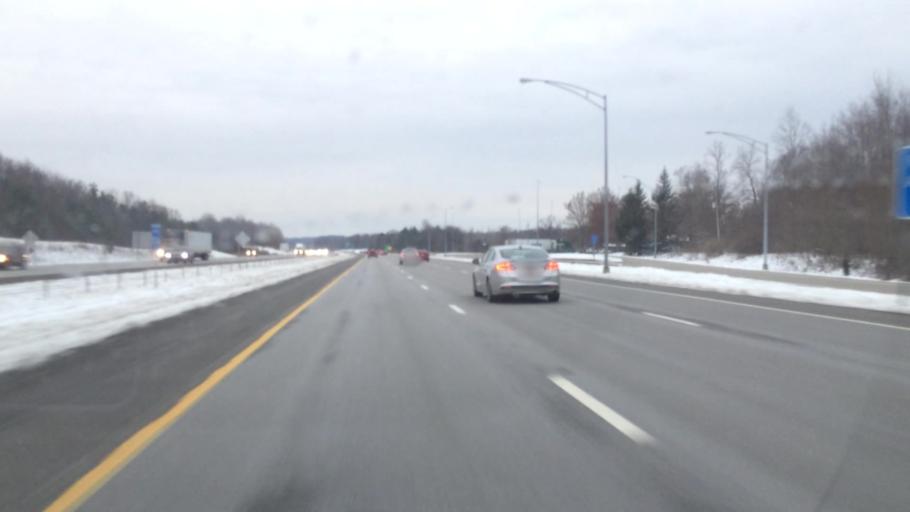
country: US
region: Ohio
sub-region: Medina County
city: Brunswick
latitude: 41.2123
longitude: -81.7938
